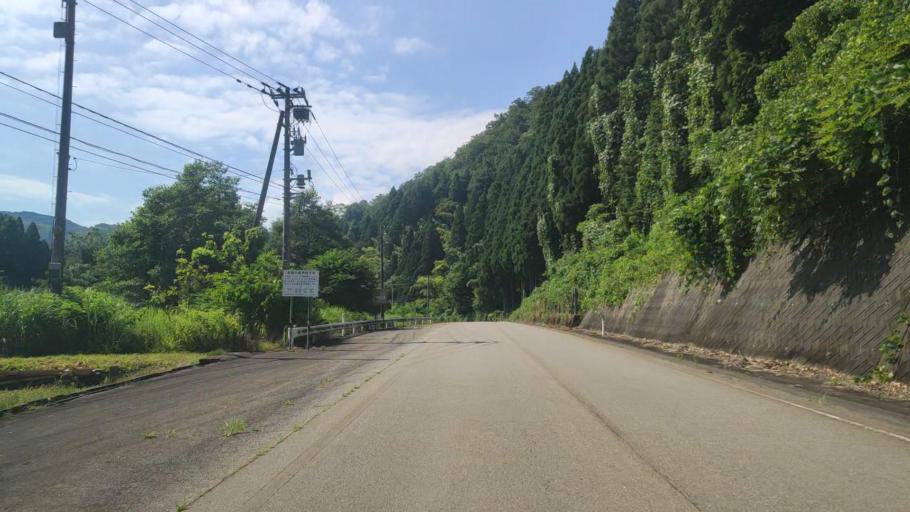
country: JP
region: Ishikawa
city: Komatsu
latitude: 36.3266
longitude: 136.5289
